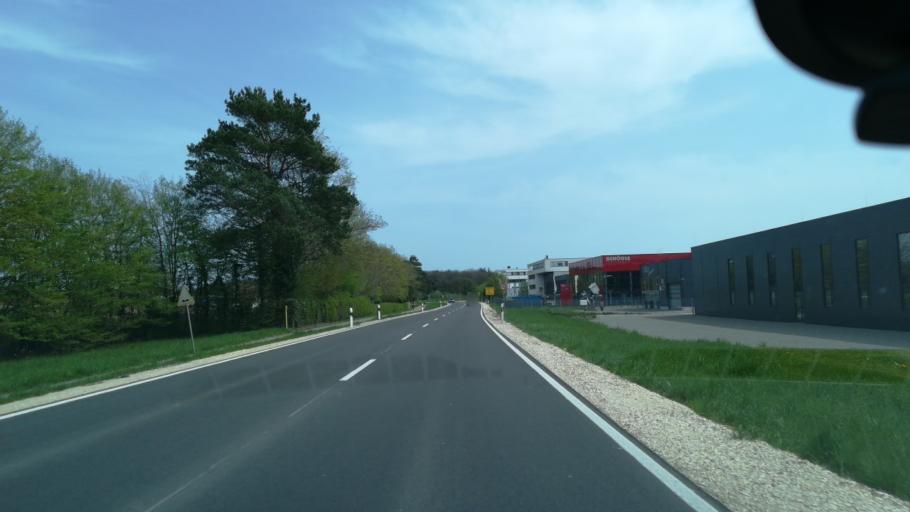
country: DE
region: Baden-Wuerttemberg
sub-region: Freiburg Region
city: Singen
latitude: 47.7609
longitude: 8.8867
